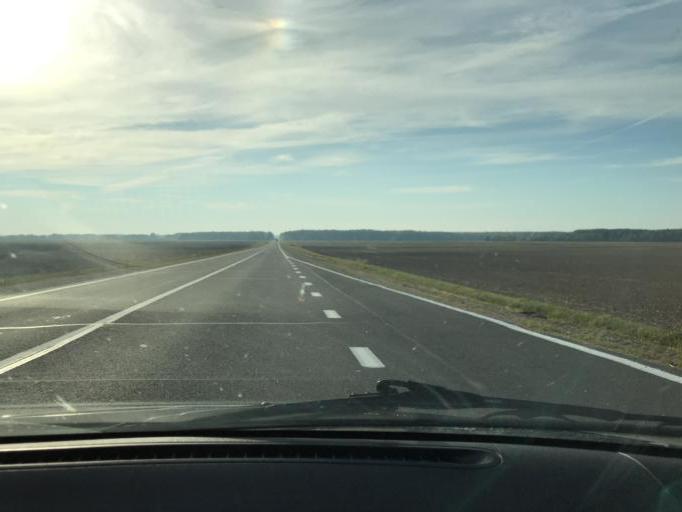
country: BY
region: Brest
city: Horad Pinsk
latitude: 52.1619
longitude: 25.9655
